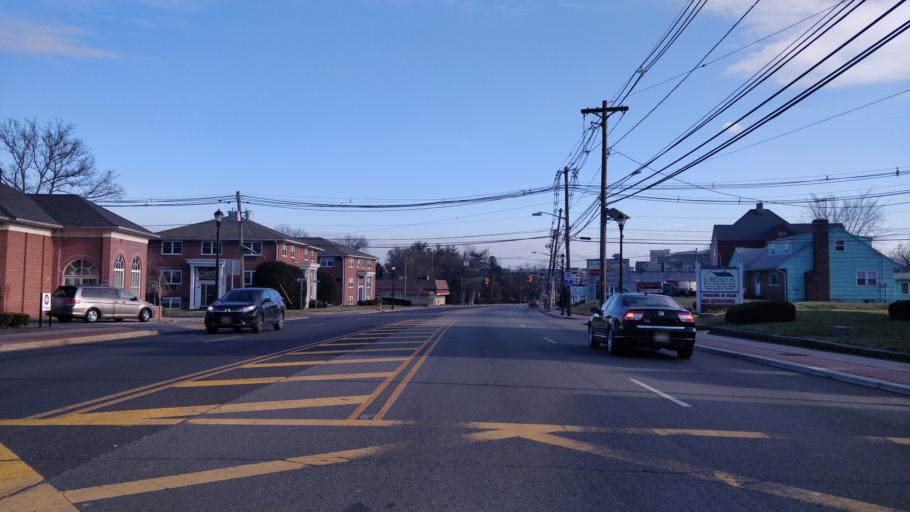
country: US
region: New Jersey
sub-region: Union County
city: Hillside
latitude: 40.6866
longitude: -74.2409
